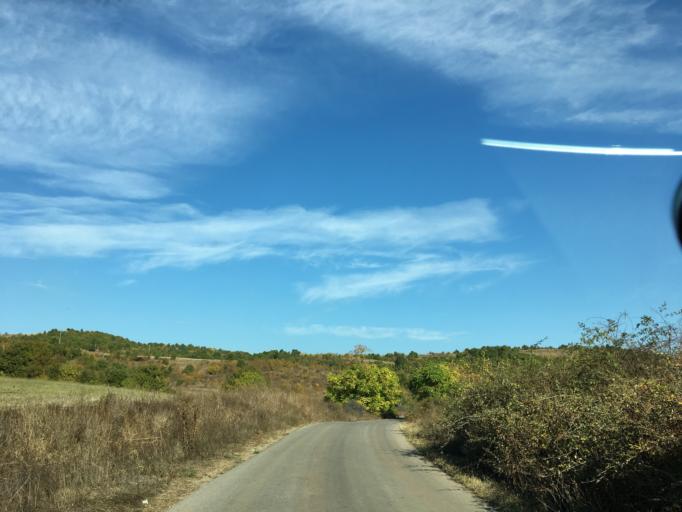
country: BG
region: Khaskovo
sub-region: Obshtina Ivaylovgrad
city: Ivaylovgrad
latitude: 41.4017
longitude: 26.1235
